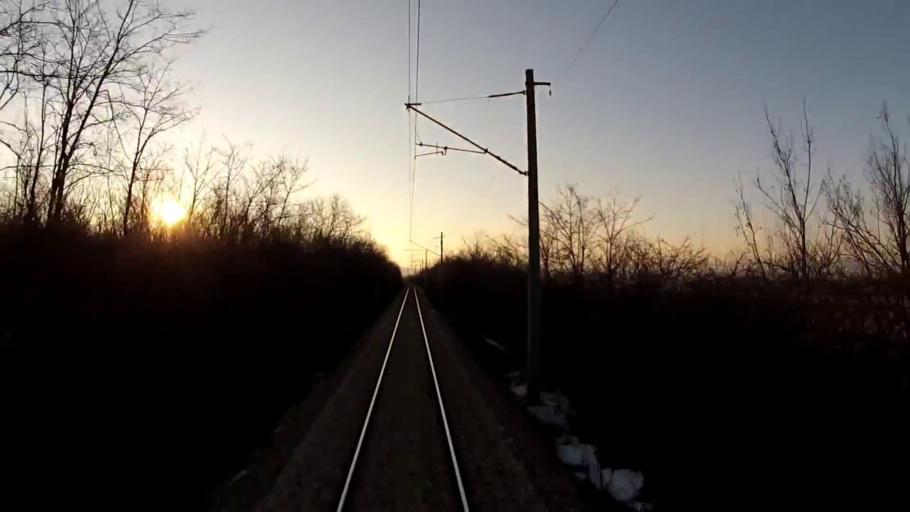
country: BG
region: Sofiya
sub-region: Obshtina Dragoman
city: Dragoman
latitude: 42.8988
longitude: 22.9575
